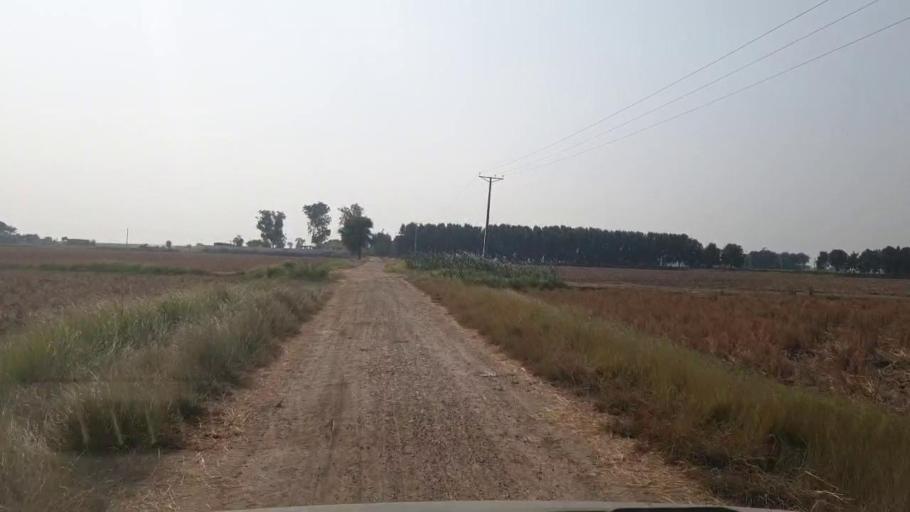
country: PK
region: Sindh
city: Bulri
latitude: 25.0195
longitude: 68.3886
